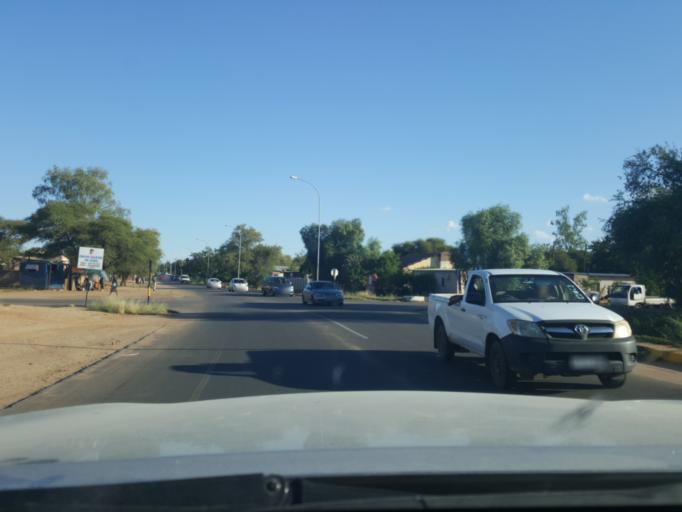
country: BW
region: South East
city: Gaborone
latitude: -24.6216
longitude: 25.9435
